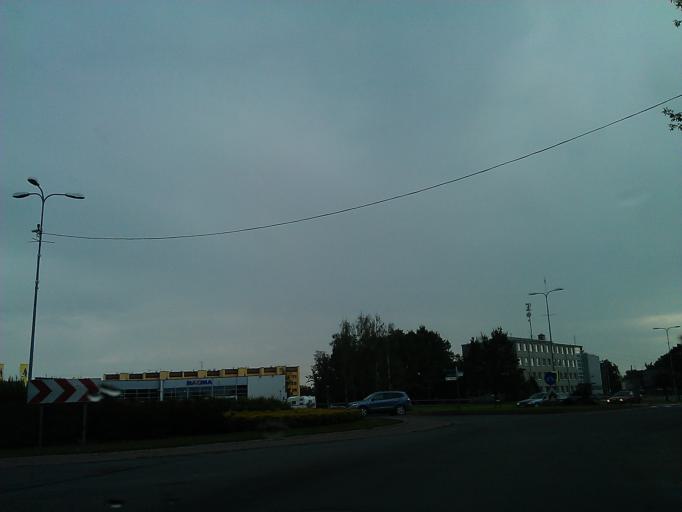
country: LV
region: Bauskas Rajons
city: Bauska
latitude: 56.4073
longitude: 24.1871
